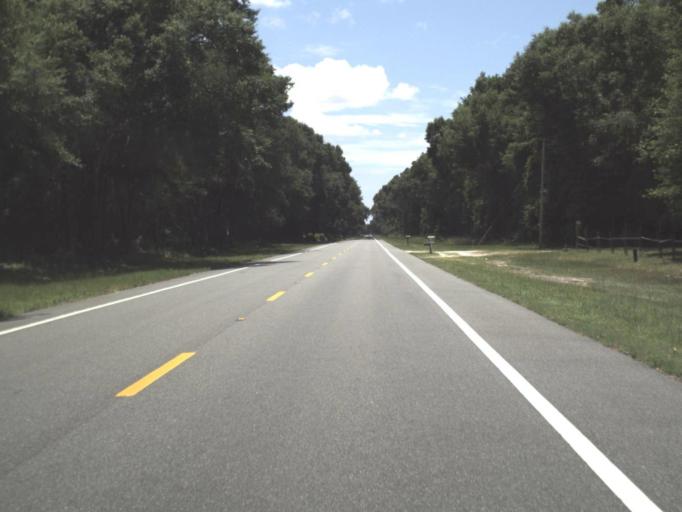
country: US
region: Florida
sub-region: Dixie County
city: Cross City
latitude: 29.8556
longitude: -82.9626
